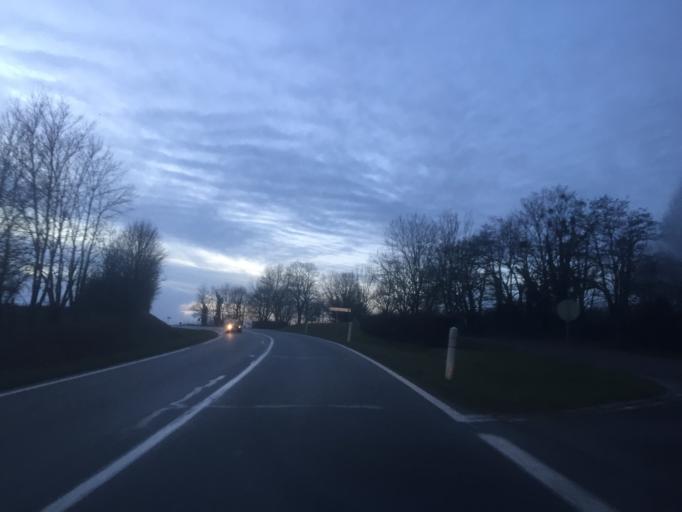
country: FR
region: Franche-Comte
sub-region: Departement du Jura
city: Orchamps
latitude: 47.1367
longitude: 5.5775
